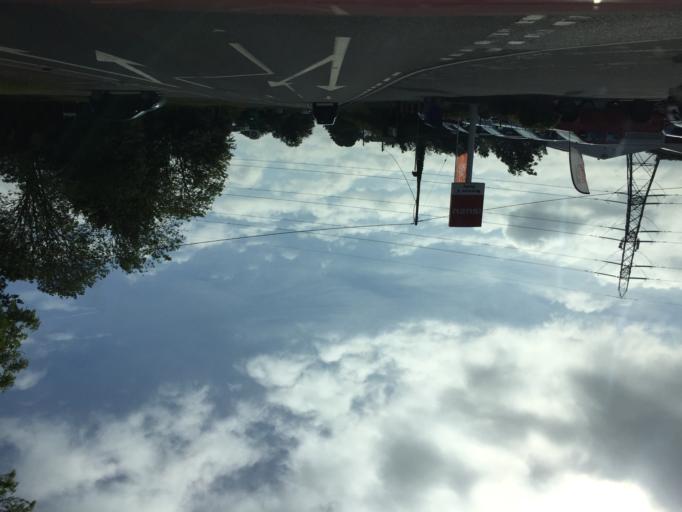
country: GB
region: England
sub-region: Northamptonshire
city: Towcester
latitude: 52.1057
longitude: -0.9408
